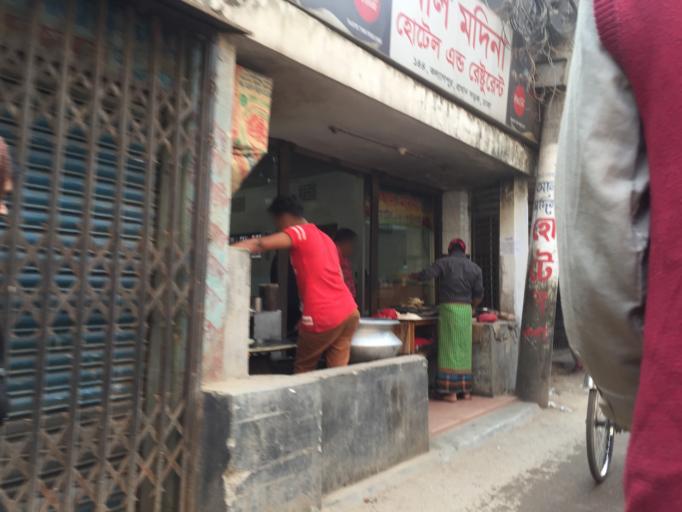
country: BD
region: Dhaka
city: Azimpur
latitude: 23.7812
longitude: 90.3604
